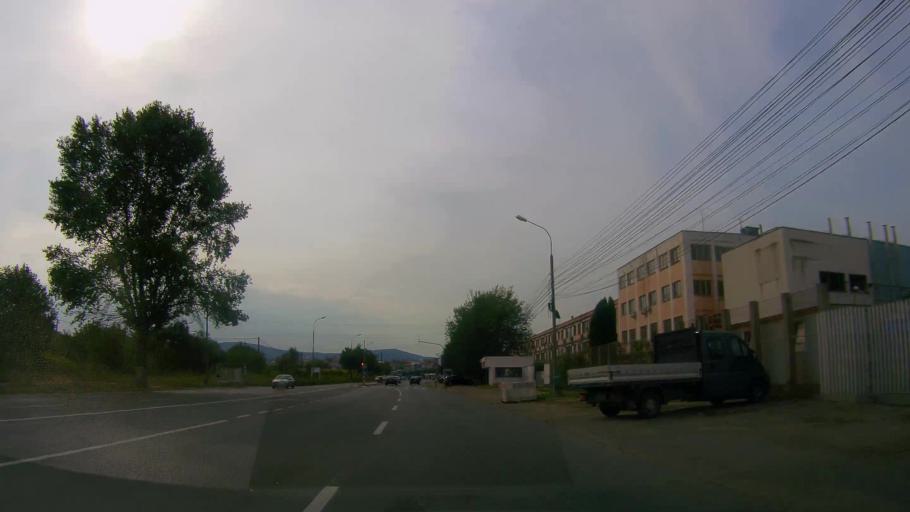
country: RO
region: Salaj
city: Zalau
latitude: 47.2113
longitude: 23.0437
